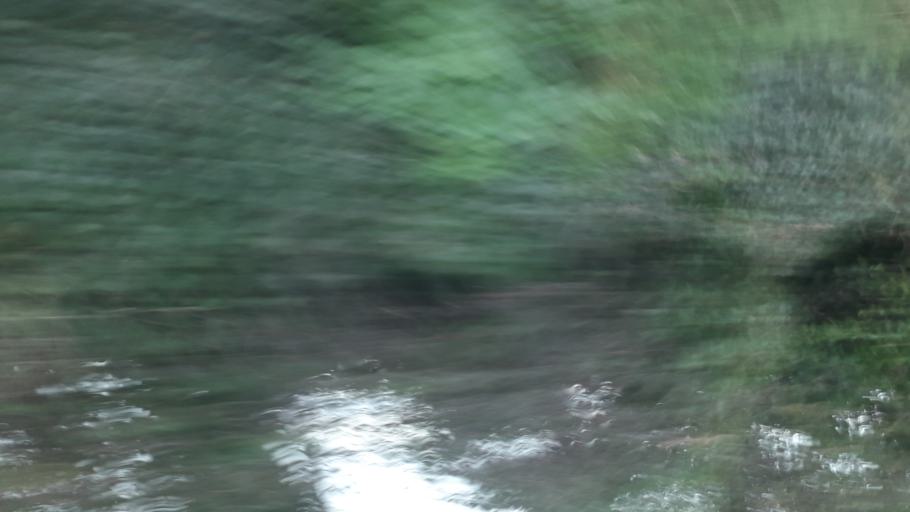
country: IE
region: Leinster
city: An Ros
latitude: 53.5179
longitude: -6.1233
